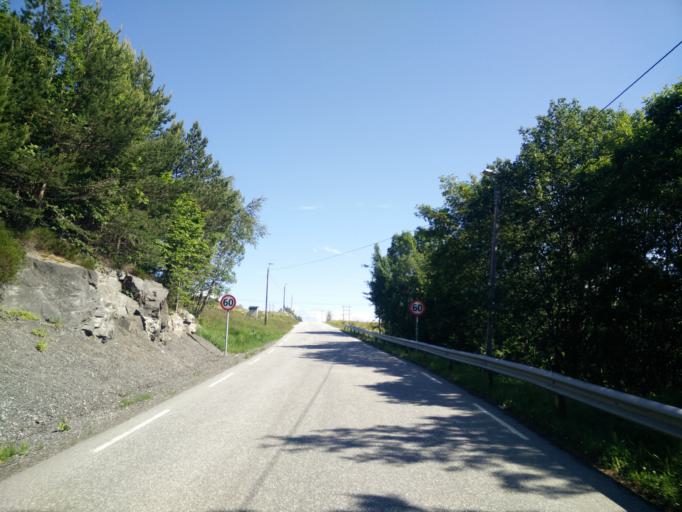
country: NO
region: More og Romsdal
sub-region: Kristiansund
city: Rensvik
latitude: 63.0440
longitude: 7.8515
